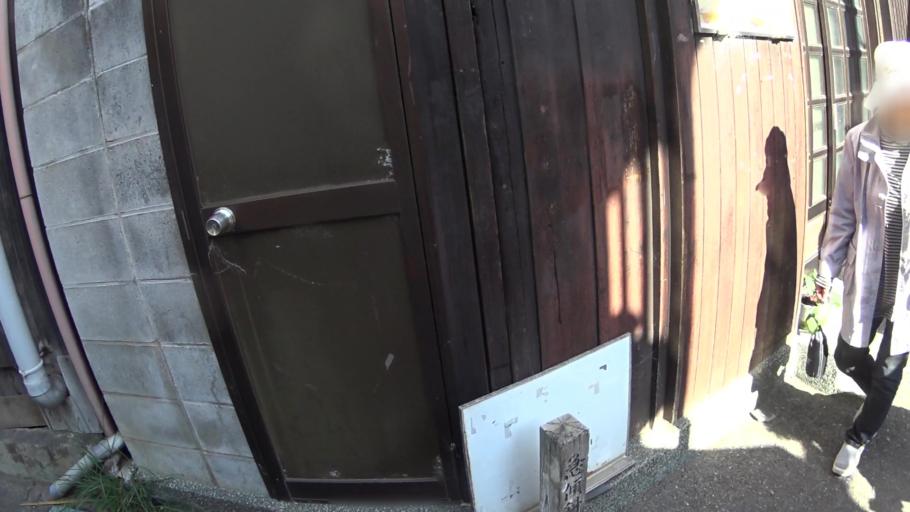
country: JP
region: Wakayama
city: Minato
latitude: 34.1894
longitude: 135.1445
